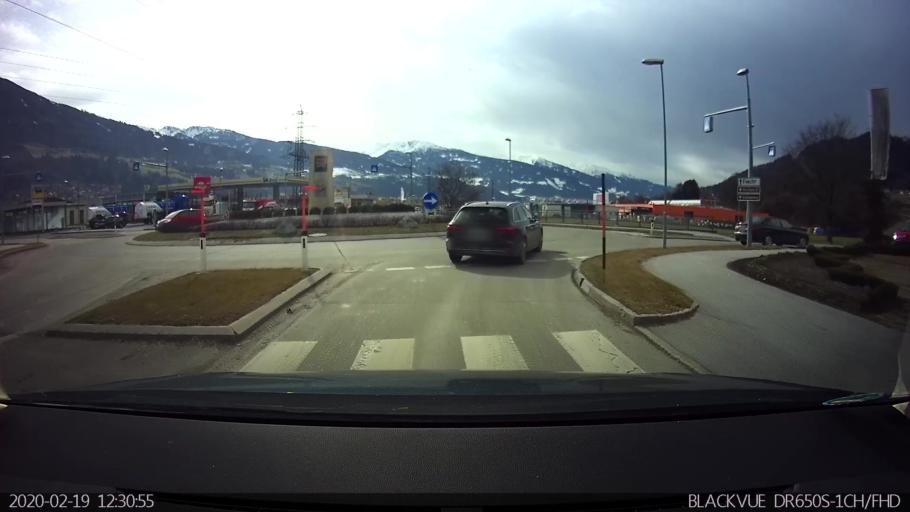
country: AT
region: Tyrol
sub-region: Politischer Bezirk Schwaz
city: Schwaz
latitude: 47.3535
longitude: 11.7002
